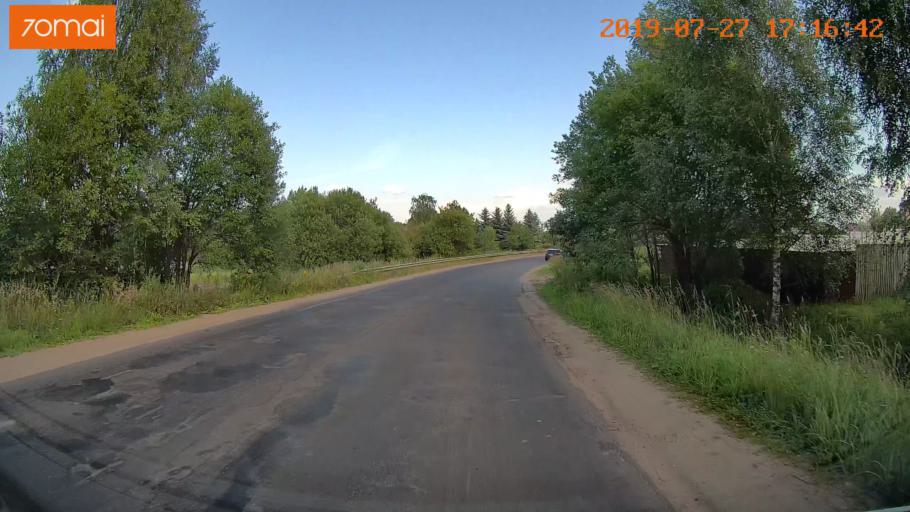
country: RU
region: Ivanovo
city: Novo-Talitsy
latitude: 57.0432
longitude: 40.8888
